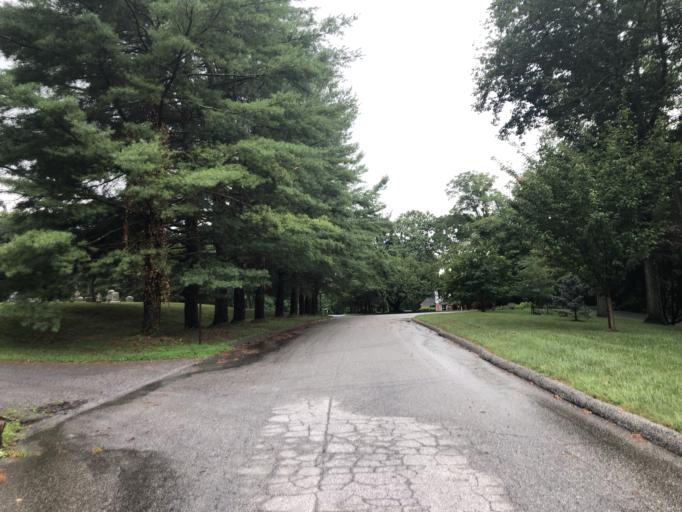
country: US
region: Maryland
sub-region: Baltimore County
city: Mays Chapel
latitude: 39.4369
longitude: -76.6867
